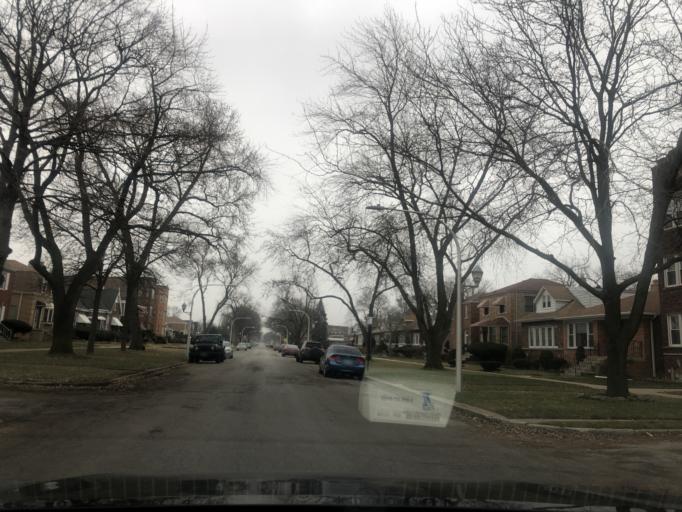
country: US
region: Illinois
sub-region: Cook County
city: Evergreen Park
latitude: 41.7435
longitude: -87.6196
